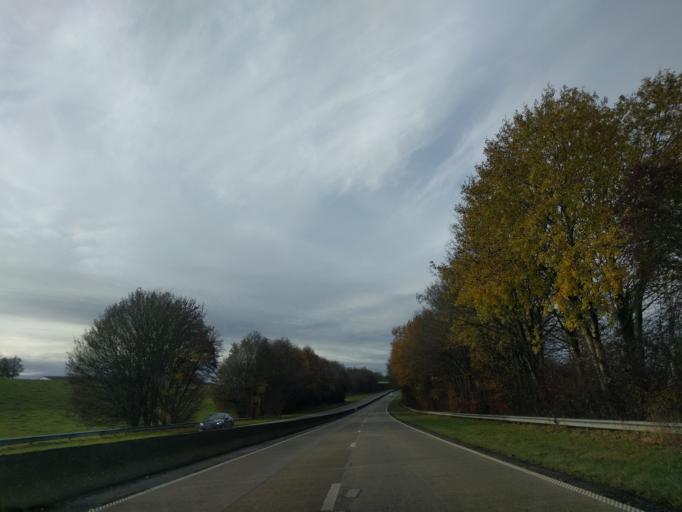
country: BE
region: Wallonia
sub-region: Province de Namur
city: Houyet
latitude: 50.2483
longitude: 5.0097
